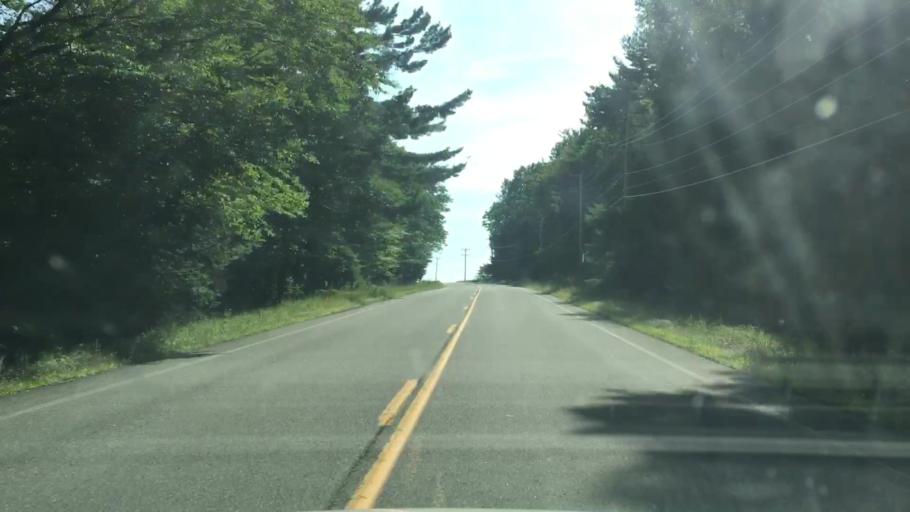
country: US
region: Maine
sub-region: Penobscot County
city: Lincoln
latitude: 45.4022
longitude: -68.5072
